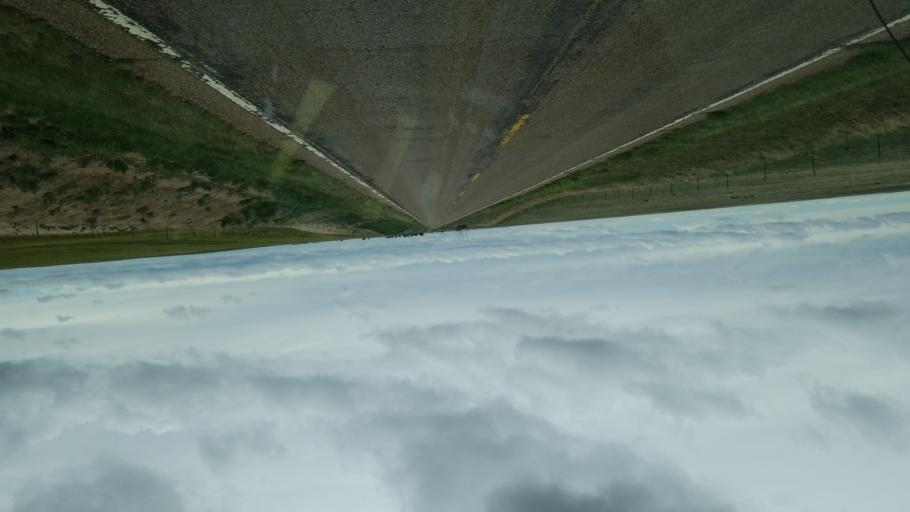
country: US
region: Colorado
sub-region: Lincoln County
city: Hugo
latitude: 38.8518
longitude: -103.6736
